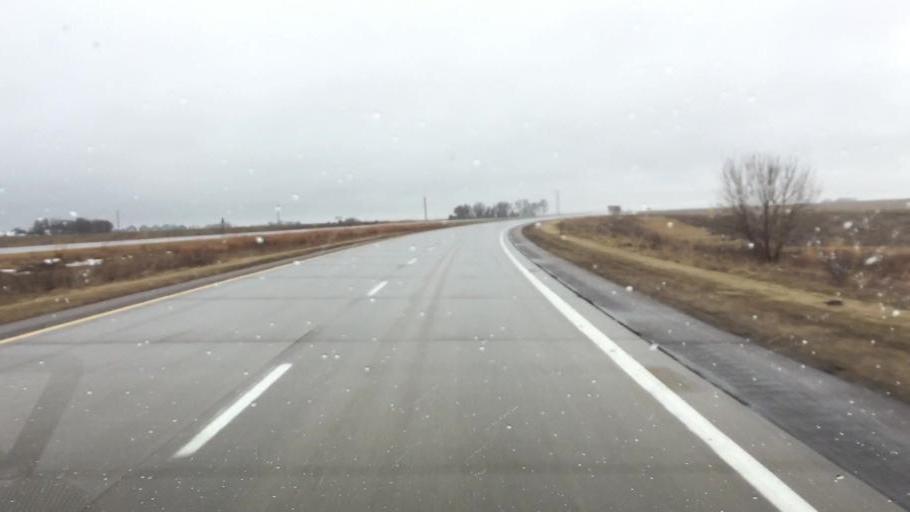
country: US
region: Iowa
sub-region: O'Brien County
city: Sheldon
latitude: 43.0674
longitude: -95.8973
